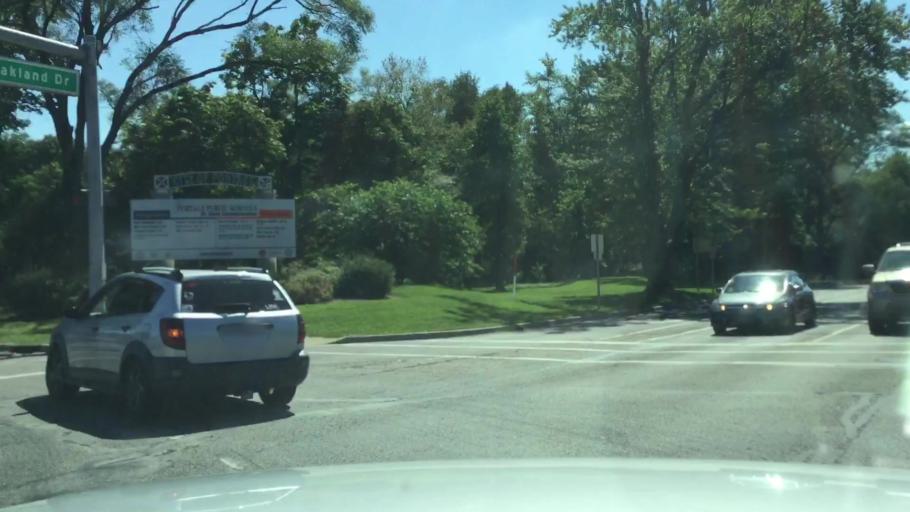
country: US
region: Michigan
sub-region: Kalamazoo County
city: Portage
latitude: 42.2301
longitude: -85.6139
